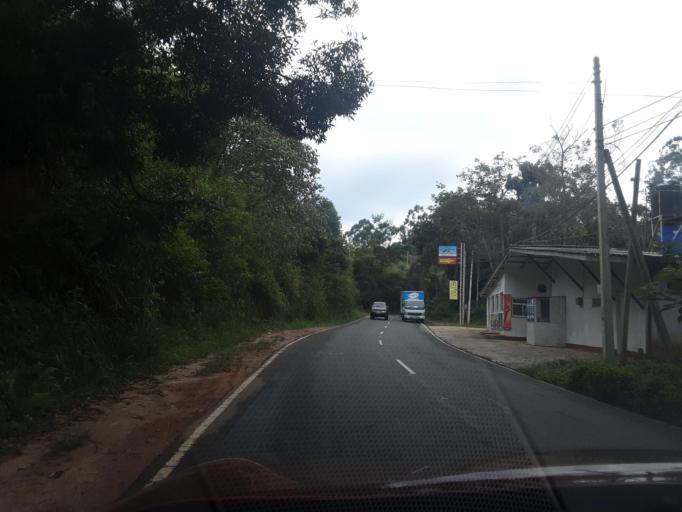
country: LK
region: Uva
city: Haputale
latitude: 6.8550
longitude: 80.9683
